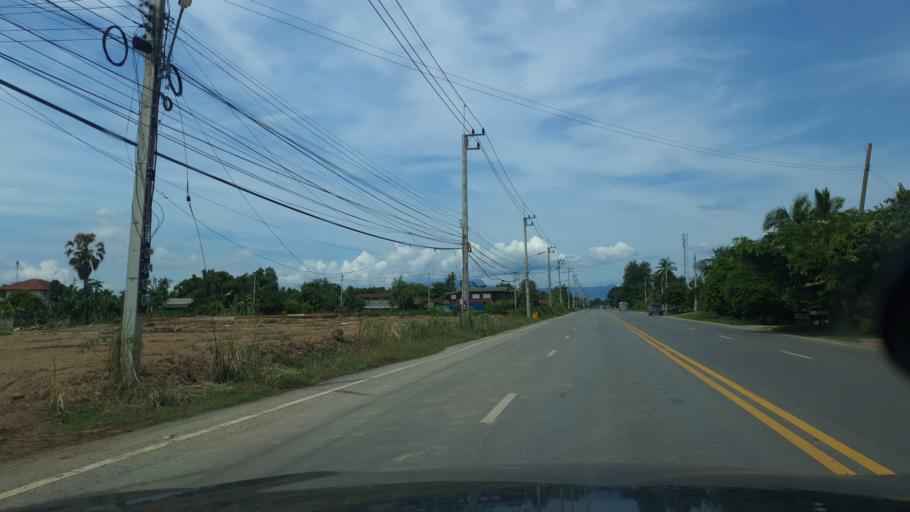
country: TH
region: Sukhothai
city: Sukhothai
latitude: 17.0577
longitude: 99.8254
